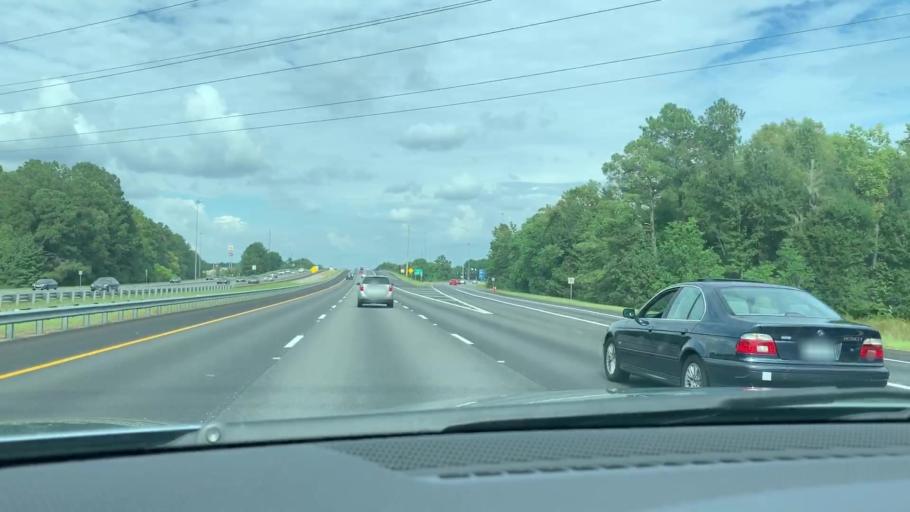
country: US
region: Georgia
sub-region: Chatham County
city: Port Wentworth
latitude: 32.1867
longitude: -81.1984
